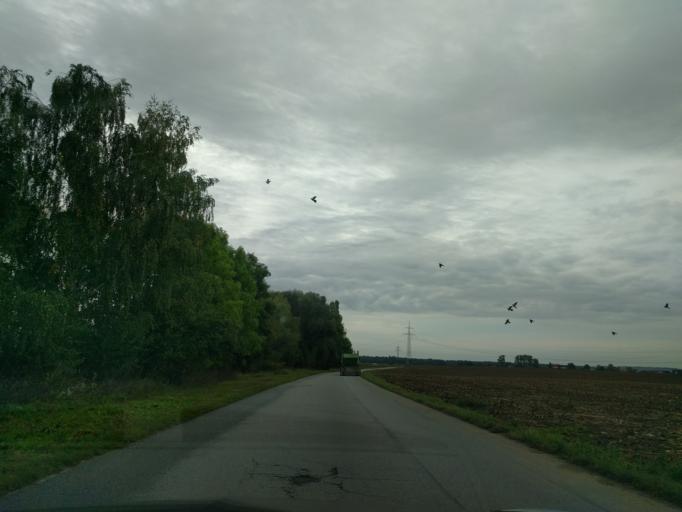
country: DE
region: Bavaria
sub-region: Lower Bavaria
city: Otzing
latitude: 48.7724
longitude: 12.8376
